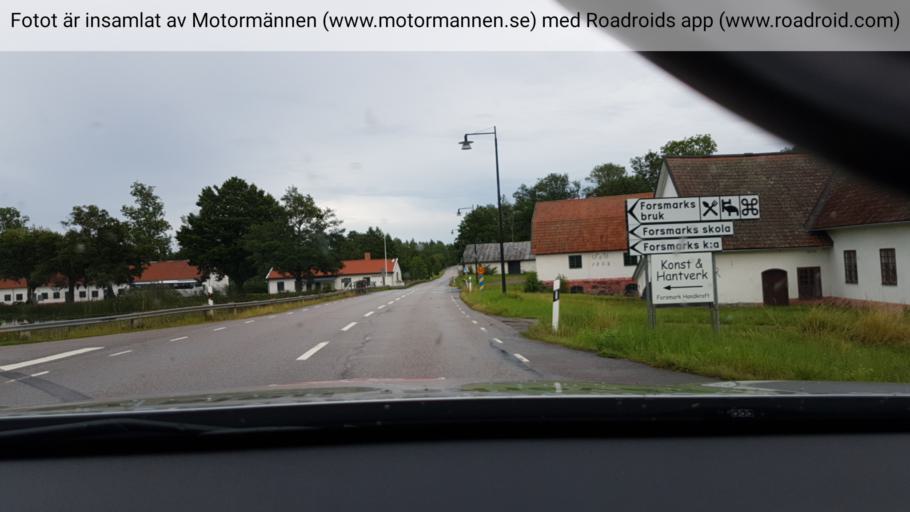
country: SE
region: Uppsala
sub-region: Osthammars Kommun
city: Gimo
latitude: 60.3697
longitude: 18.1530
